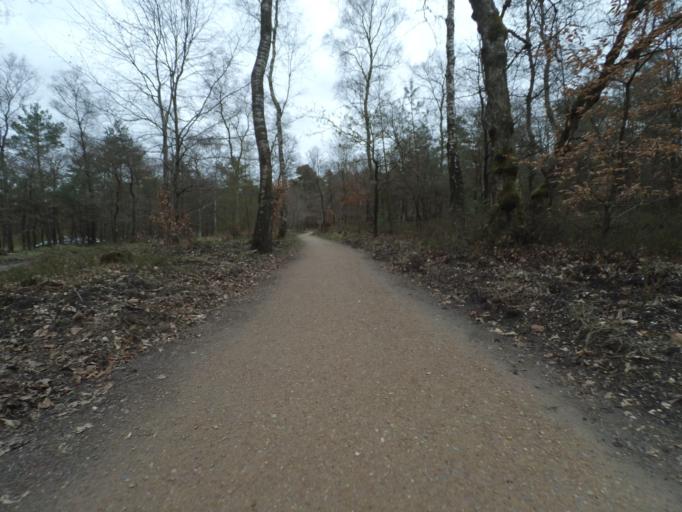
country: NL
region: Gelderland
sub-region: Gemeente Apeldoorn
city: Loenen
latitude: 52.1001
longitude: 5.9956
